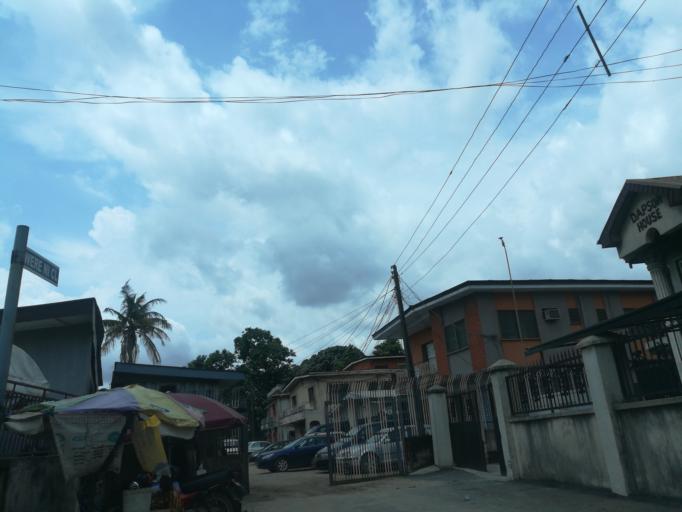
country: NG
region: Lagos
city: Somolu
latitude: 6.5396
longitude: 3.3658
